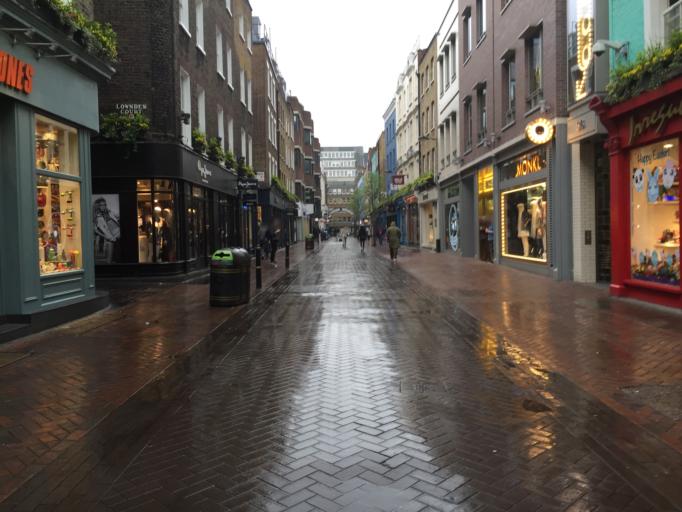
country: GB
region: England
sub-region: Greater London
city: London
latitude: 51.5136
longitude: -0.1393
